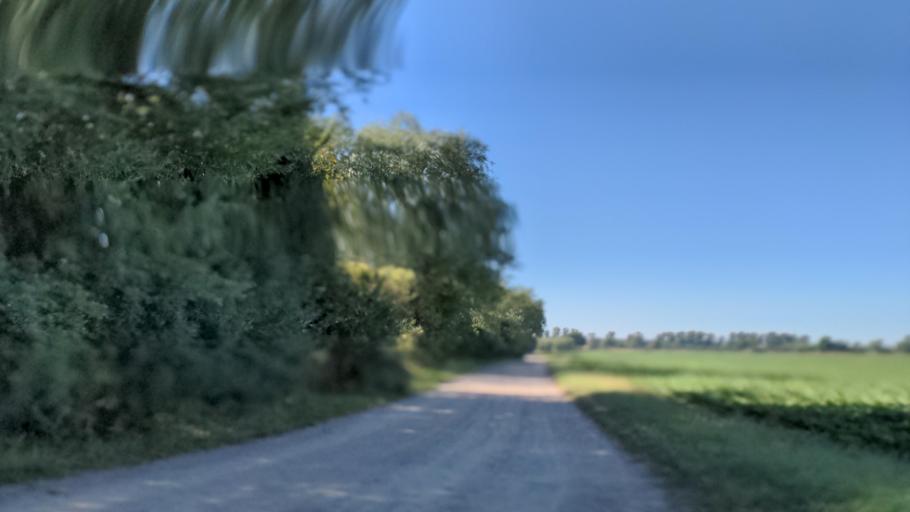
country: DE
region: Mecklenburg-Vorpommern
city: Ostseebad Boltenhagen
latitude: 53.9530
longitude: 11.2373
